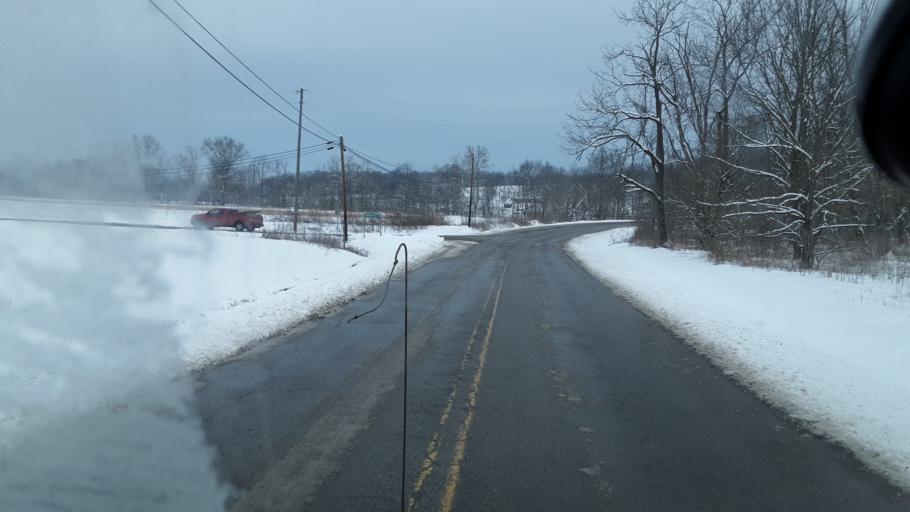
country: US
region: Ohio
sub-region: Perry County
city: Somerset
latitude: 39.8818
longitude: -82.2156
